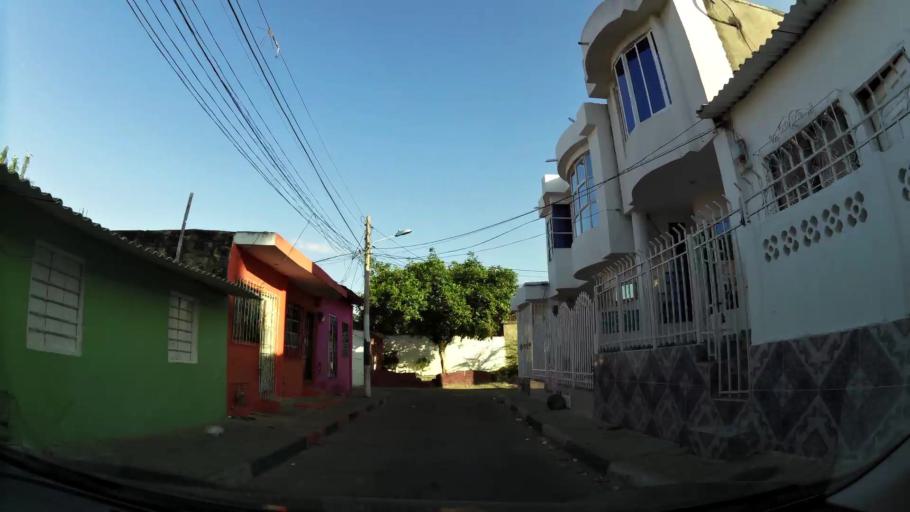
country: CO
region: Bolivar
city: Cartagena
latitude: 10.4021
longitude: -75.5151
